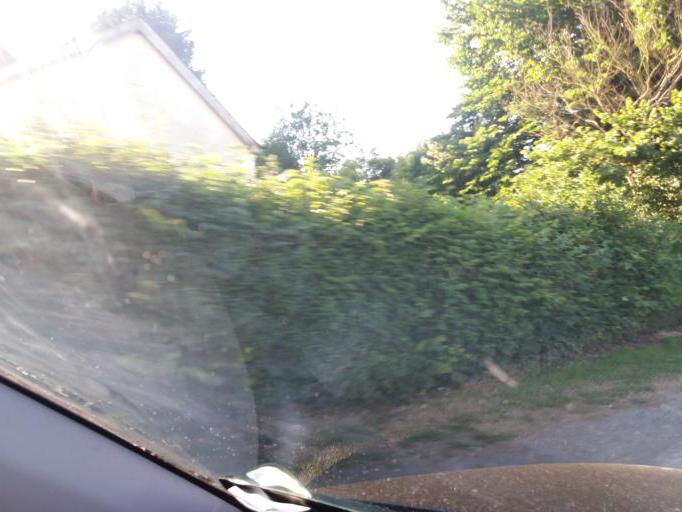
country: IE
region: Leinster
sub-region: An Mhi
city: Ashbourne
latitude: 53.4737
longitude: -6.3197
